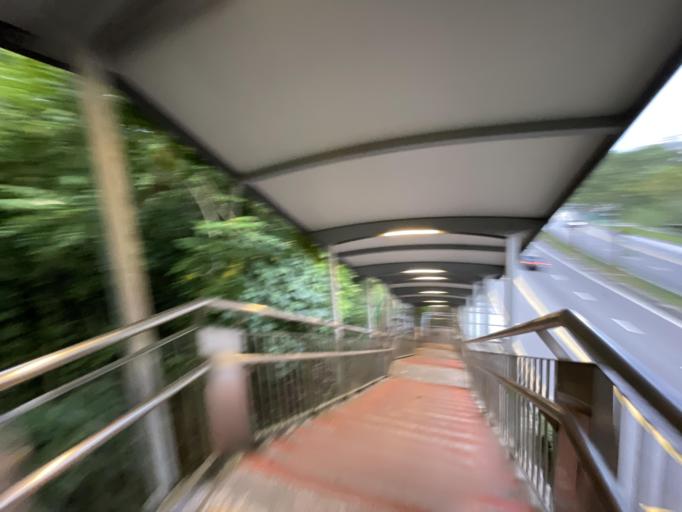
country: SG
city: Singapore
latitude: 1.3563
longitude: 103.7686
